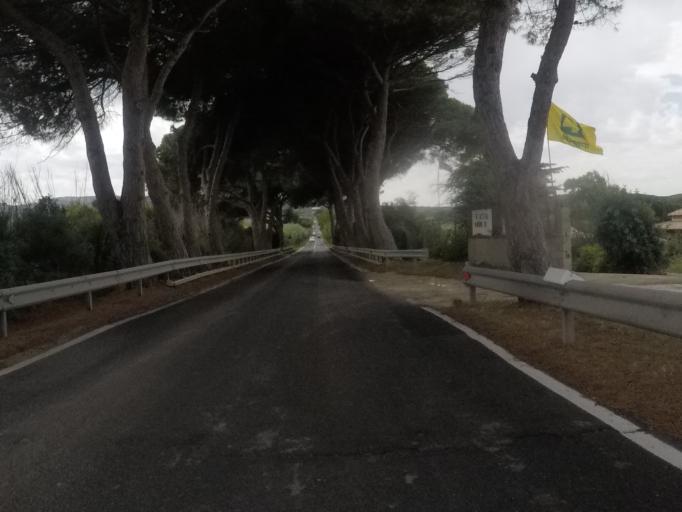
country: IT
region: Sardinia
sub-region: Provincia di Sassari
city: Sorso
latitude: 40.8333
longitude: 8.5952
